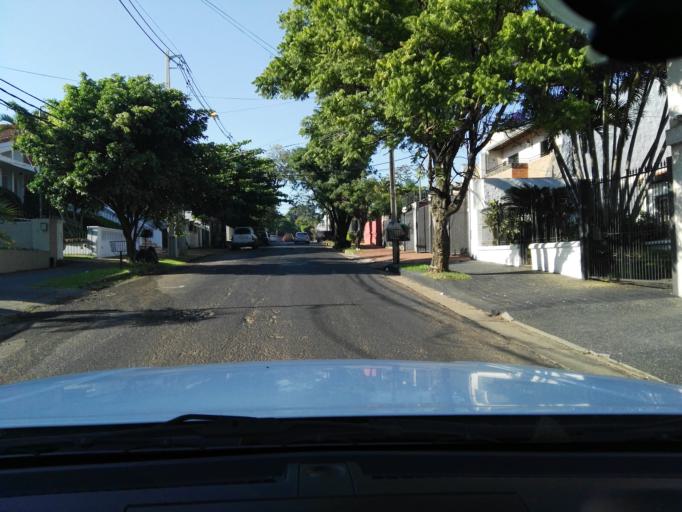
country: PY
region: Central
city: Lambare
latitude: -25.3055
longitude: -57.5769
